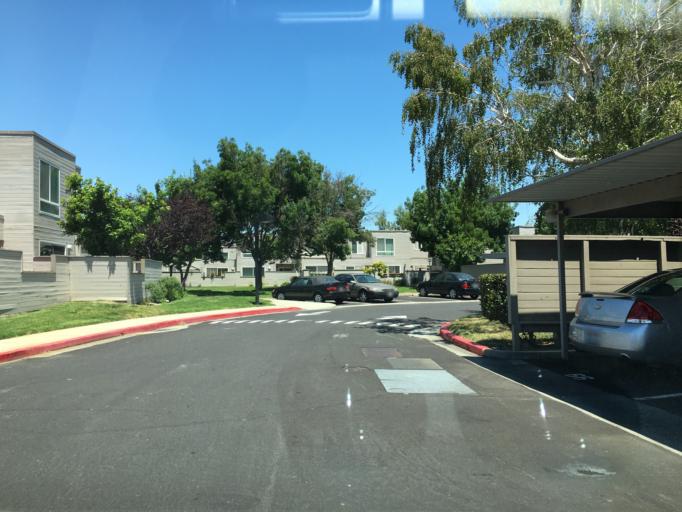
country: US
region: California
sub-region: San Mateo County
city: Redwood Shores
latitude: 37.5252
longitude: -122.2533
